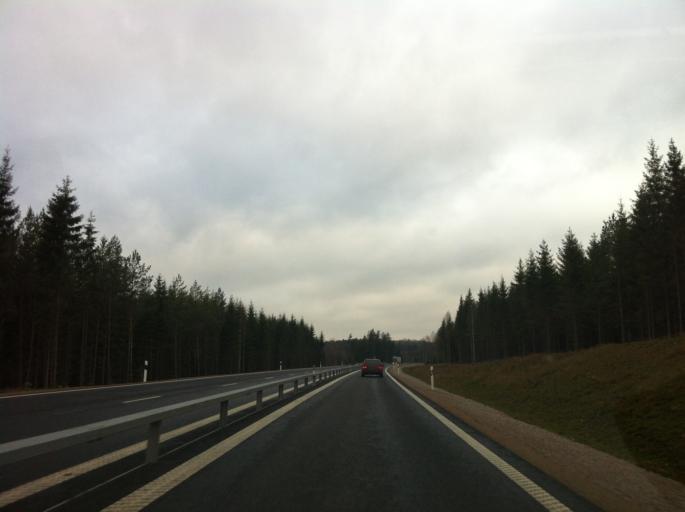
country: SE
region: Joenkoeping
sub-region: Vetlanda Kommun
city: Vetlanda
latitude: 57.4163
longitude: 15.2276
